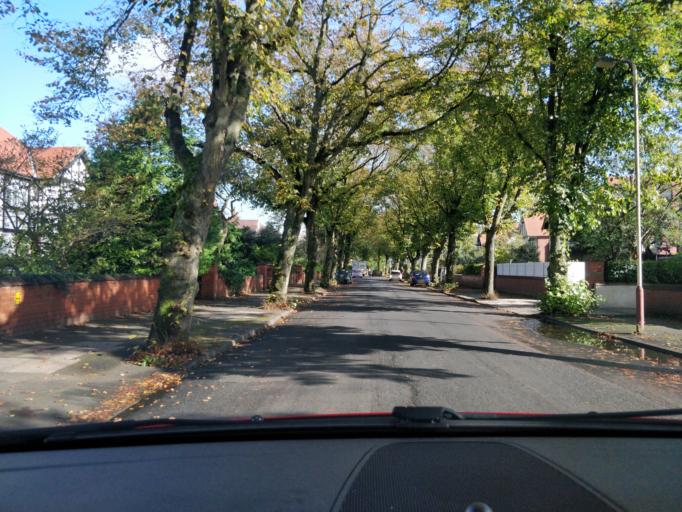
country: GB
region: England
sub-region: Sefton
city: Southport
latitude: 53.6367
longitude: -2.9879
